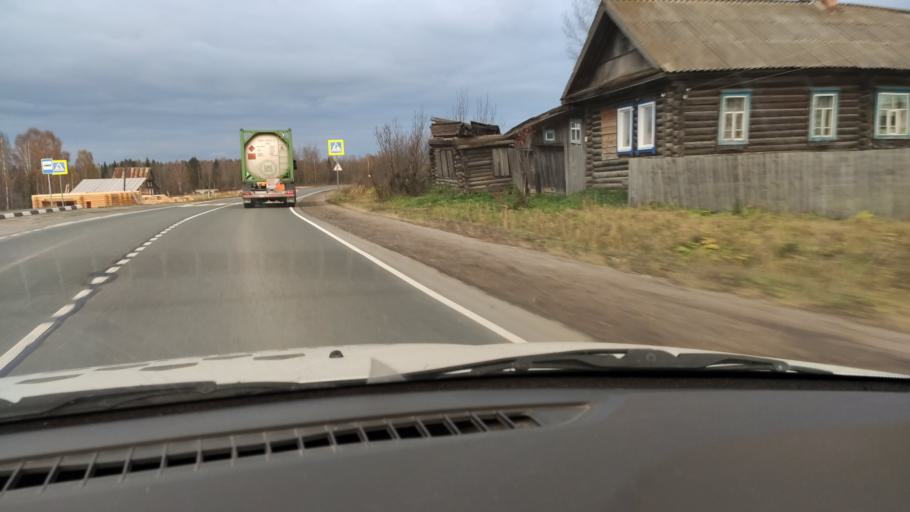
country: RU
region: Kirov
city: Belorechensk
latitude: 58.7147
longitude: 52.3291
